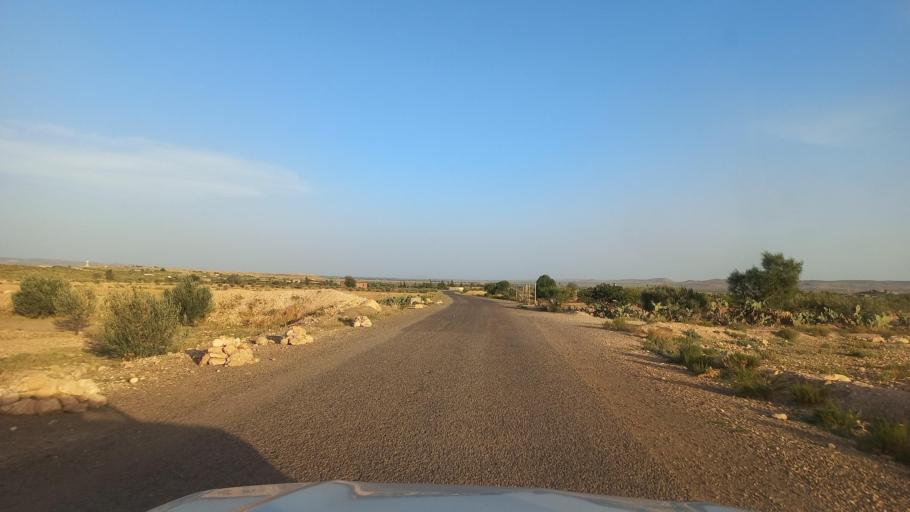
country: TN
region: Al Qasrayn
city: Kasserine
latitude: 35.2730
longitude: 8.9243
